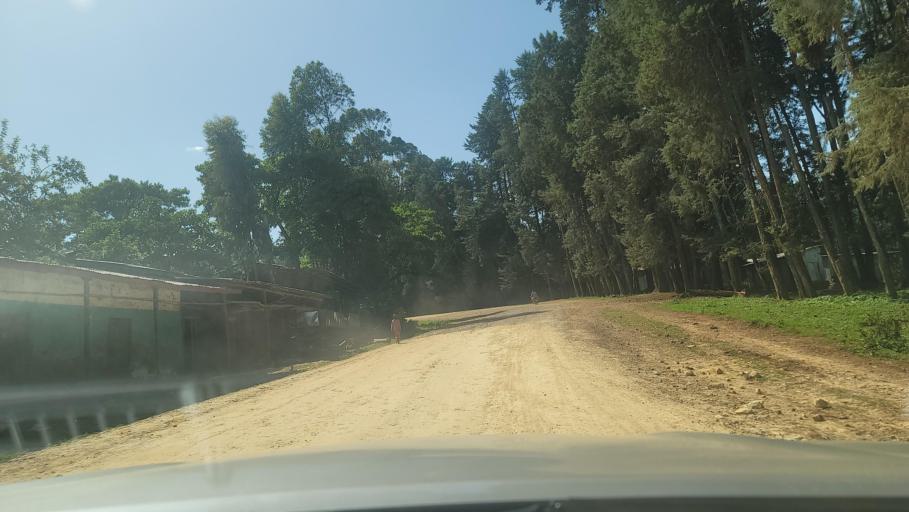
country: ET
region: Oromiya
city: Agaro
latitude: 7.7871
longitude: 36.4243
